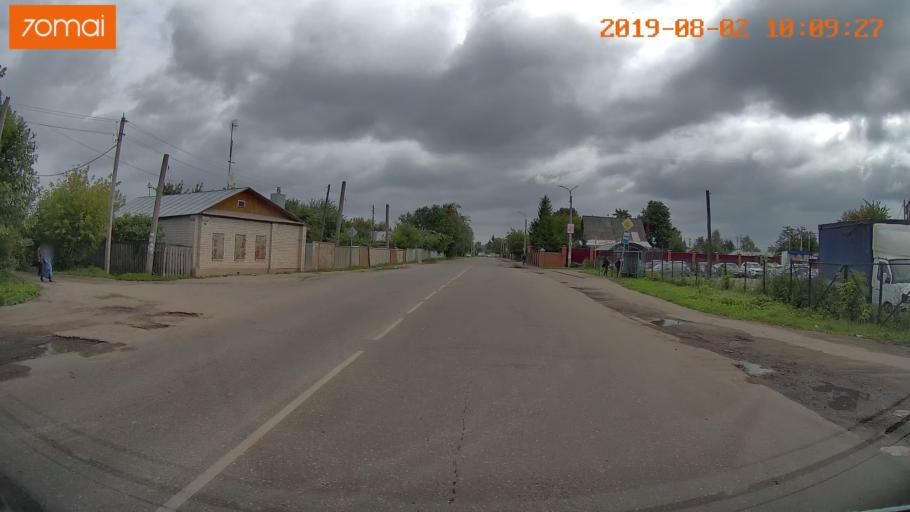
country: RU
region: Ivanovo
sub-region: Gorod Ivanovo
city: Ivanovo
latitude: 56.9880
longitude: 40.9465
